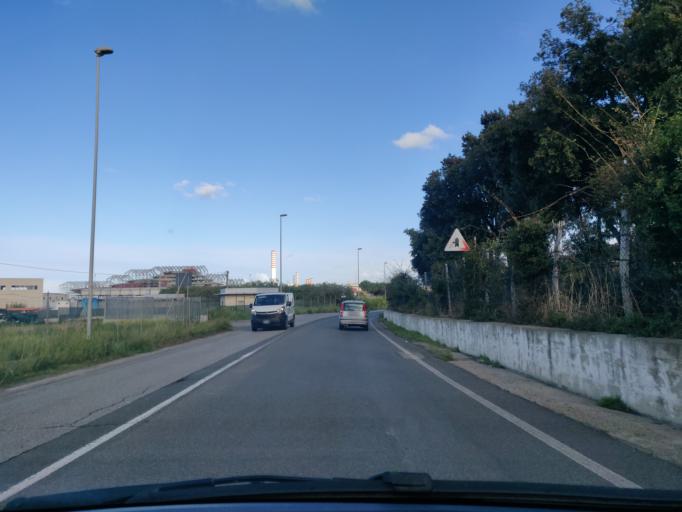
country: IT
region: Latium
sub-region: Citta metropolitana di Roma Capitale
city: Civitavecchia
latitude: 42.1090
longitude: 11.7783
